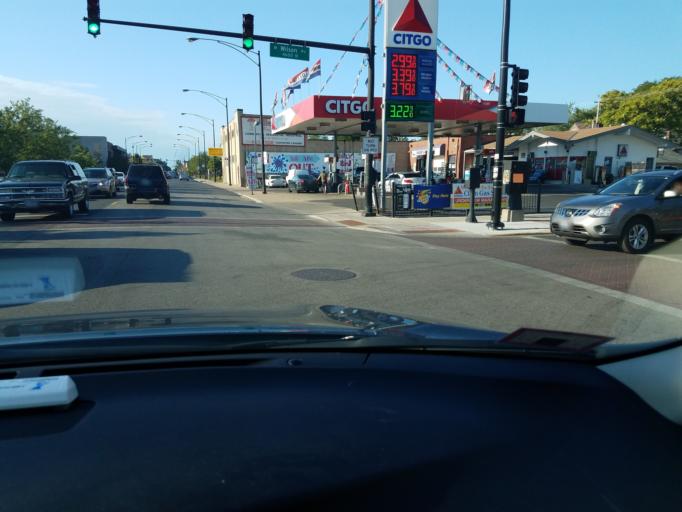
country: US
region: Illinois
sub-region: Cook County
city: Lincolnwood
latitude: 41.9645
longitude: -87.7279
